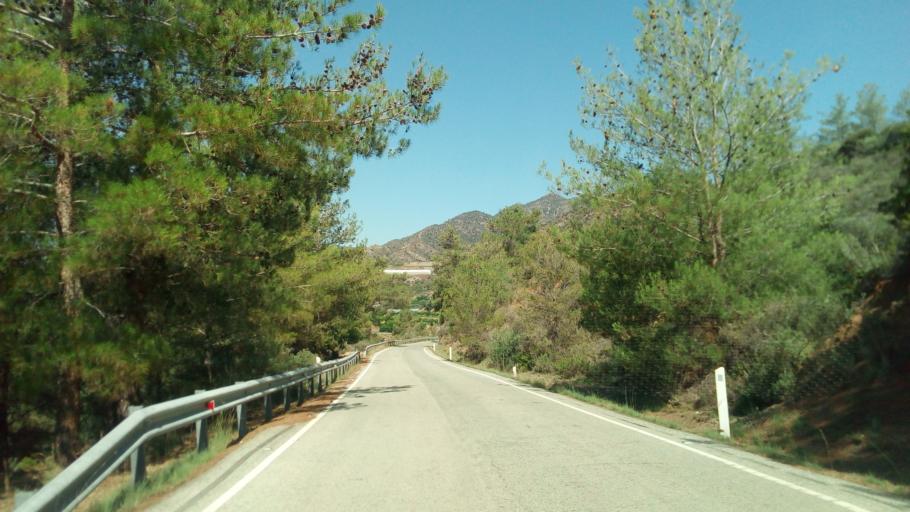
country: CY
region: Limassol
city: Parekklisha
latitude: 34.8661
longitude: 33.1825
